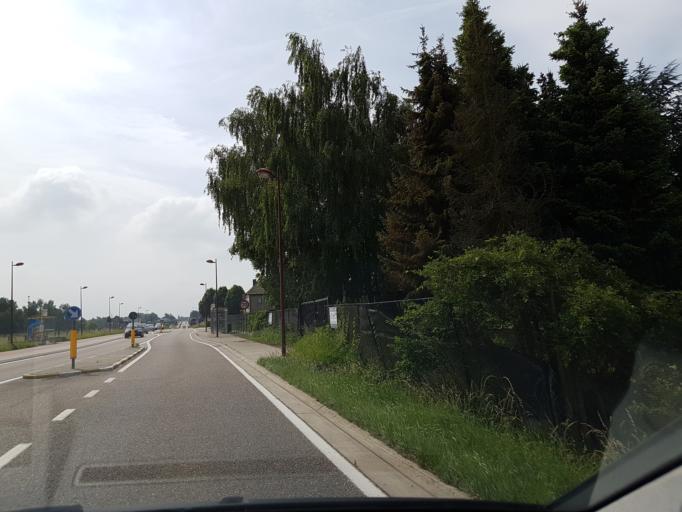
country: BE
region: Flanders
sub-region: Provincie Vlaams-Brabant
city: Asse
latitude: 50.9310
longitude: 4.1789
